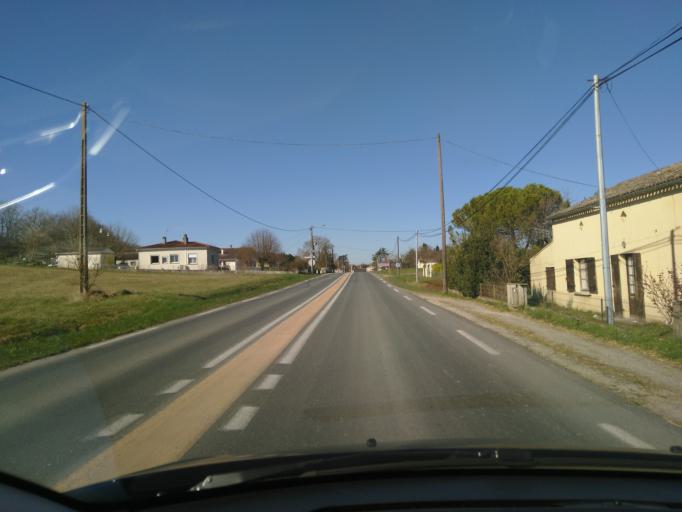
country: FR
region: Aquitaine
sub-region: Departement de la Dordogne
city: Monbazillac
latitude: 44.7544
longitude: 0.5305
